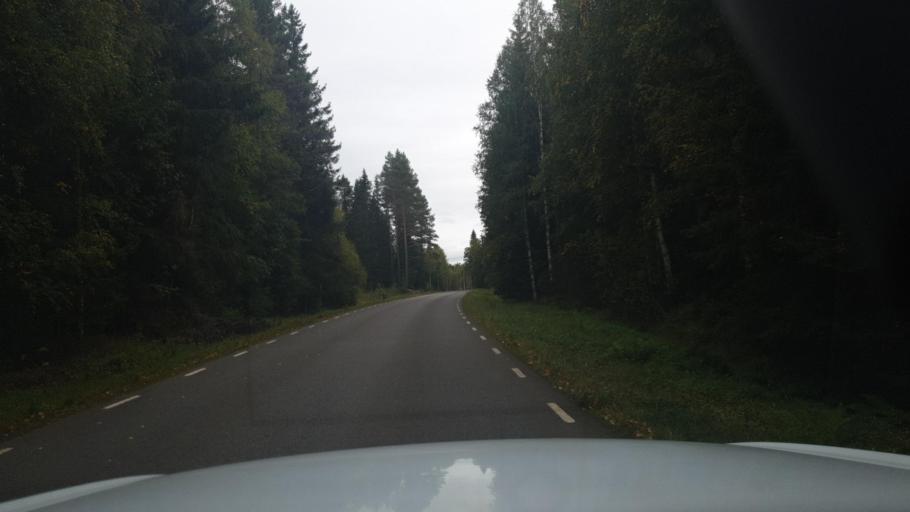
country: SE
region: Vaermland
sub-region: Torsby Kommun
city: Torsby
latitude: 60.0070
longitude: 12.6953
